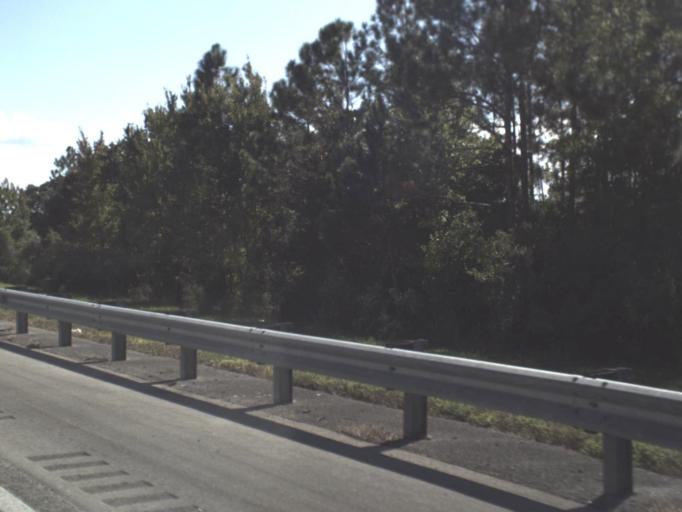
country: US
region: Florida
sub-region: Brevard County
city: June Park
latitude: 27.9121
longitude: -81.0524
